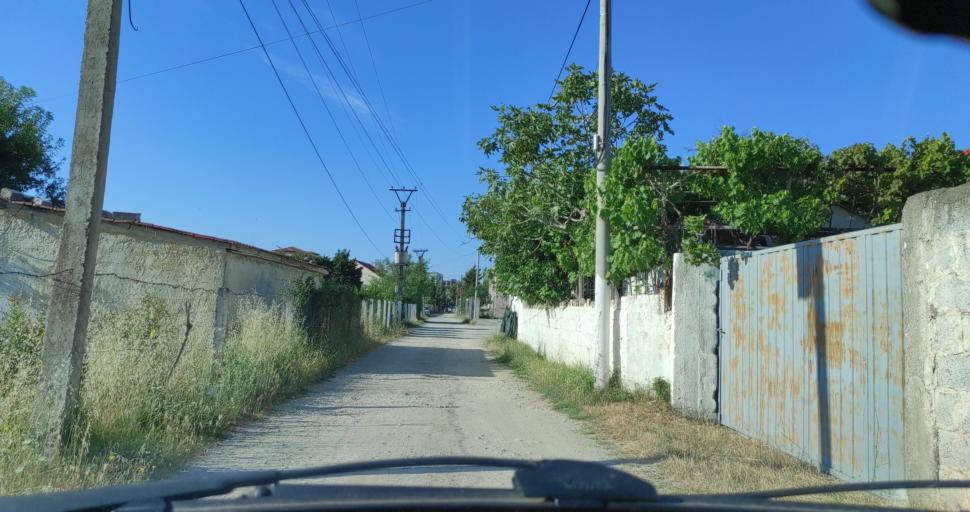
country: AL
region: Shkoder
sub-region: Rrethi i Shkodres
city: Velipoje
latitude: 41.8680
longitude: 19.4261
